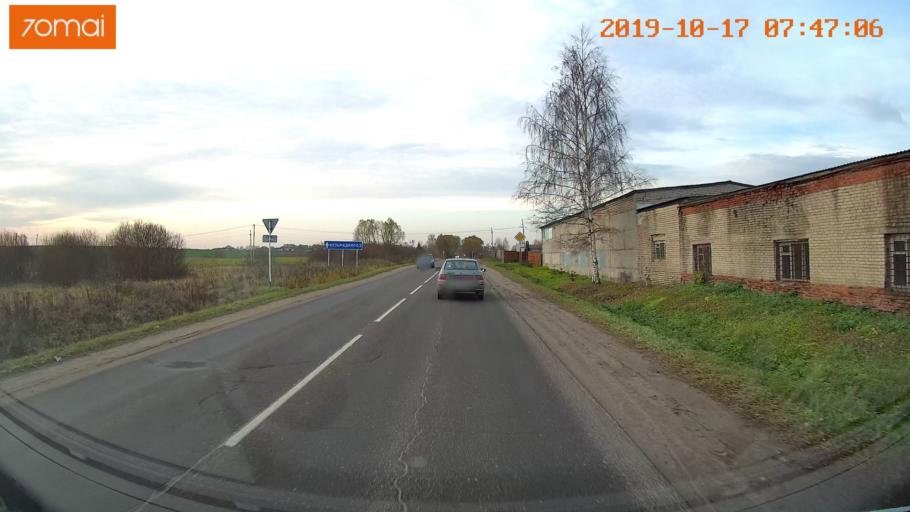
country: RU
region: Vladimir
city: Yur'yev-Pol'skiy
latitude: 56.4896
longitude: 39.6874
